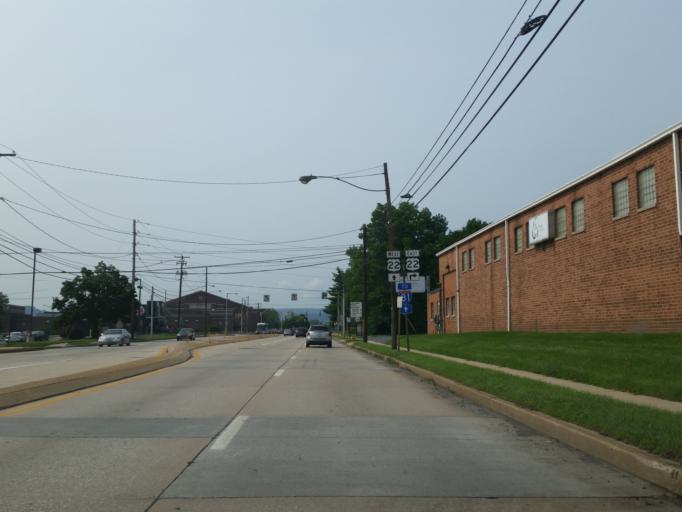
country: US
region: Pennsylvania
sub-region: Dauphin County
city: Harrisburg
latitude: 40.2813
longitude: -76.8803
